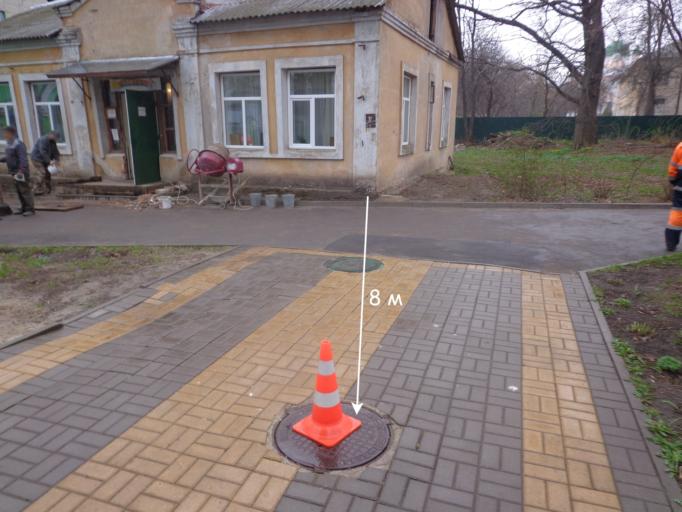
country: RU
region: Voronezj
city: Voronezh
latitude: 51.7139
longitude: 39.2308
